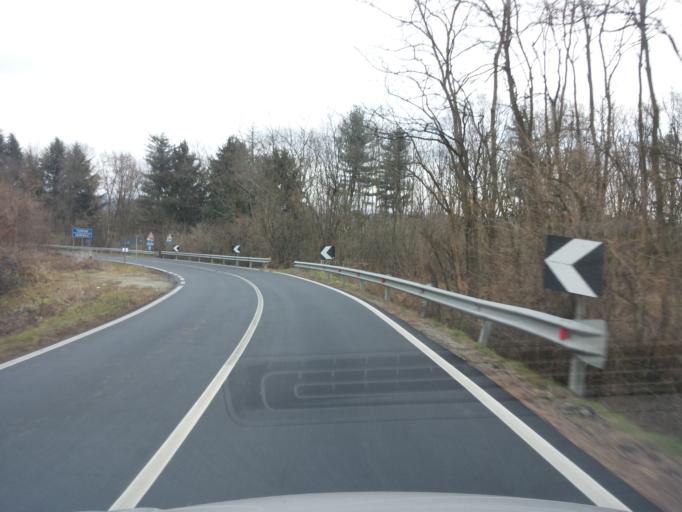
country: IT
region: Piedmont
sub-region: Provincia di Vercelli
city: Moncrivello
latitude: 45.3427
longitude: 7.9975
